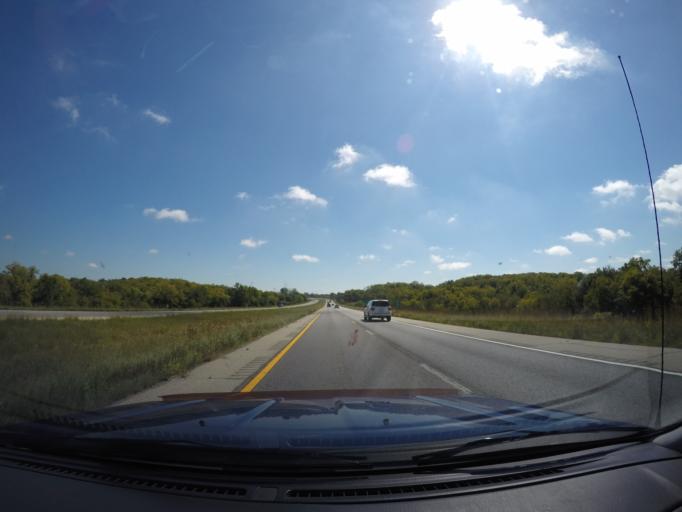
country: US
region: Kansas
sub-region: Johnson County
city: Olathe
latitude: 38.9448
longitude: -94.8759
